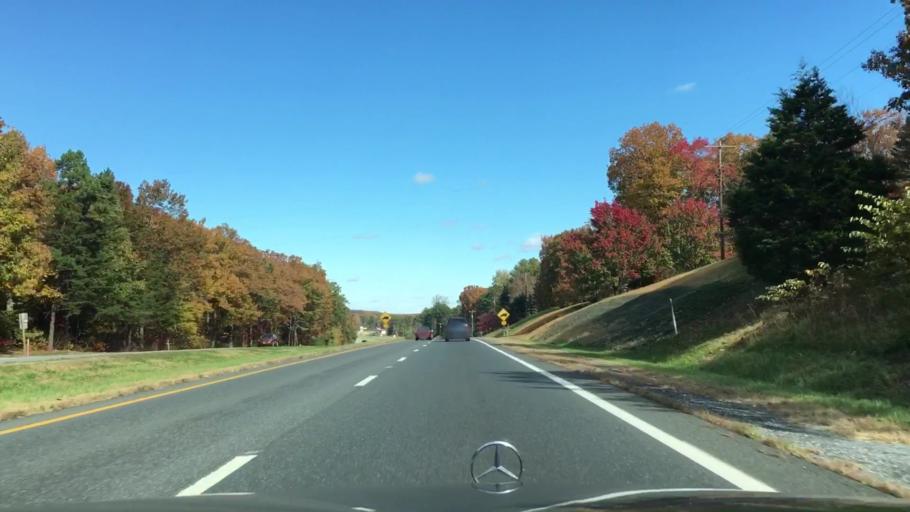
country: US
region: Virginia
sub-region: Campbell County
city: Rustburg
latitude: 37.2208
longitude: -79.1922
